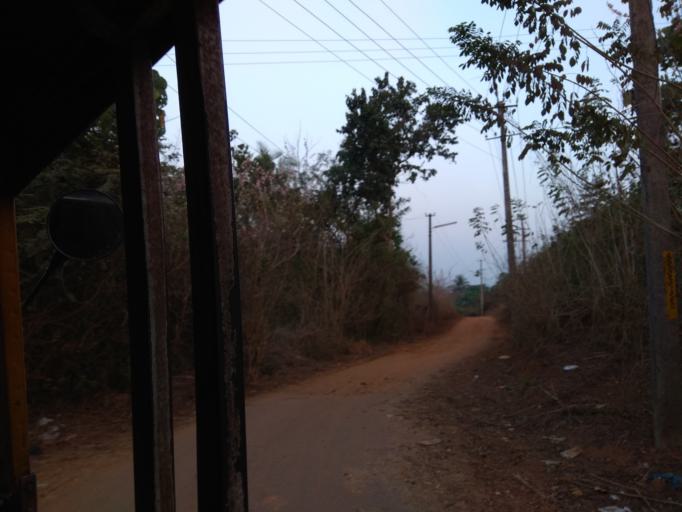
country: IN
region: Karnataka
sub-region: Dakshina Kannada
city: Mangalore
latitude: 12.9354
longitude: 74.8665
